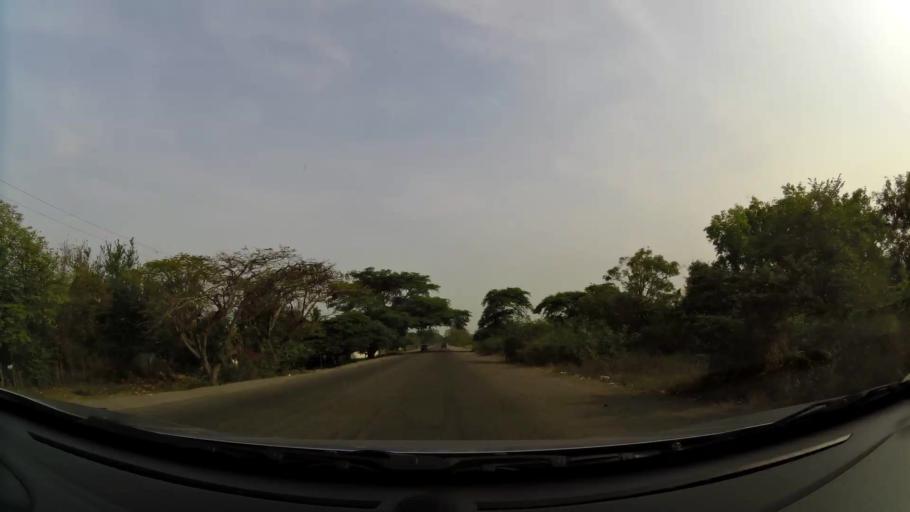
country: HN
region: Comayagua
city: Flores
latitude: 14.2841
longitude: -87.5666
